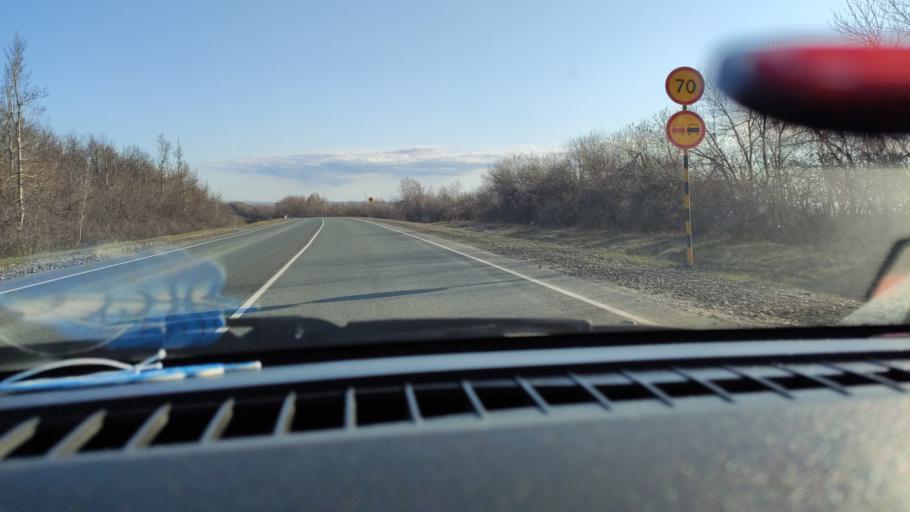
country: RU
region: Saratov
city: Dukhovnitskoye
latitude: 52.6259
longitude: 48.1797
